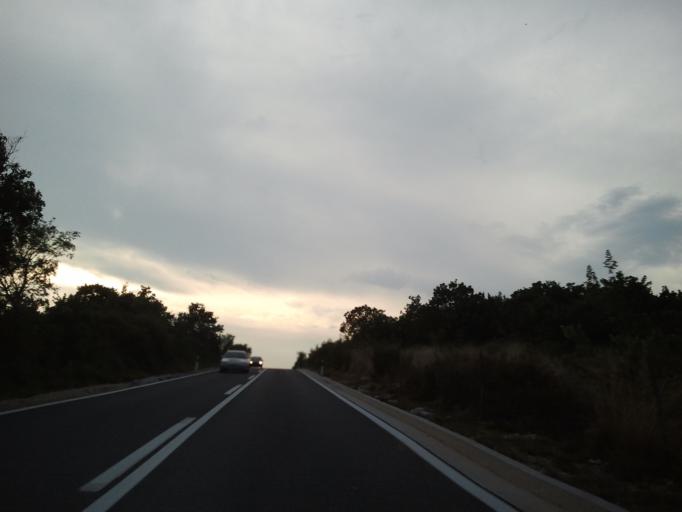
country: HR
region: Zadarska
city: Posedarje
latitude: 44.2255
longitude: 15.4374
